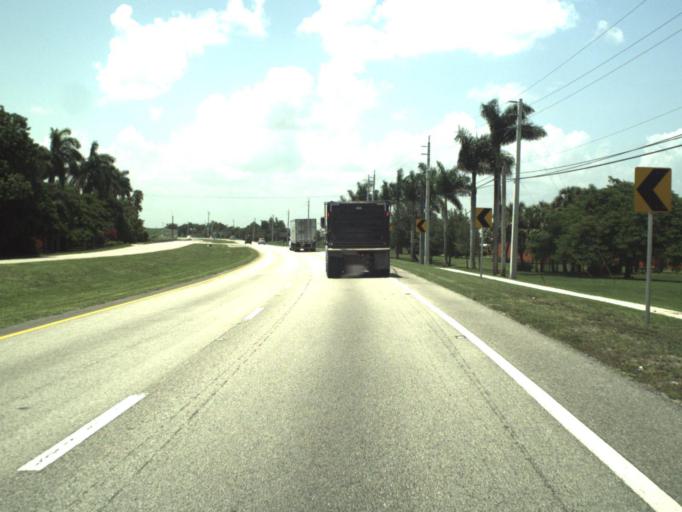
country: US
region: Florida
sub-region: Palm Beach County
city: South Bay
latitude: 26.6771
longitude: -80.7240
